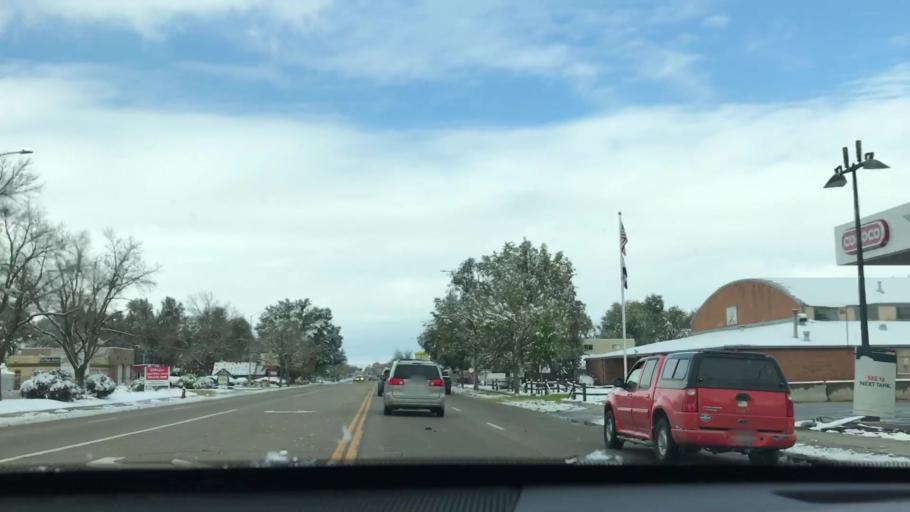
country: US
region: Colorado
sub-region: Boulder County
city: Longmont
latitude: 40.1850
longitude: -105.1023
